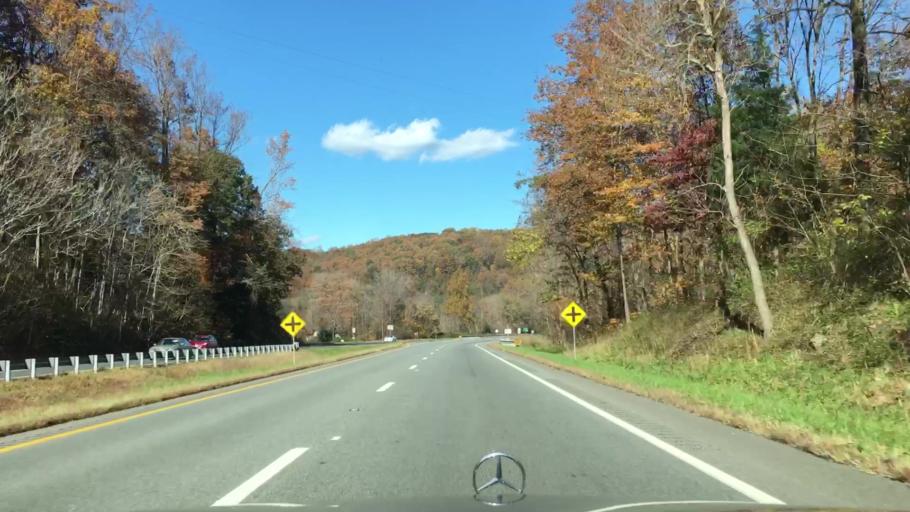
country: US
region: Virginia
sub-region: City of Charlottesville
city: Charlottesville
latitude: 38.0000
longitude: -78.5812
